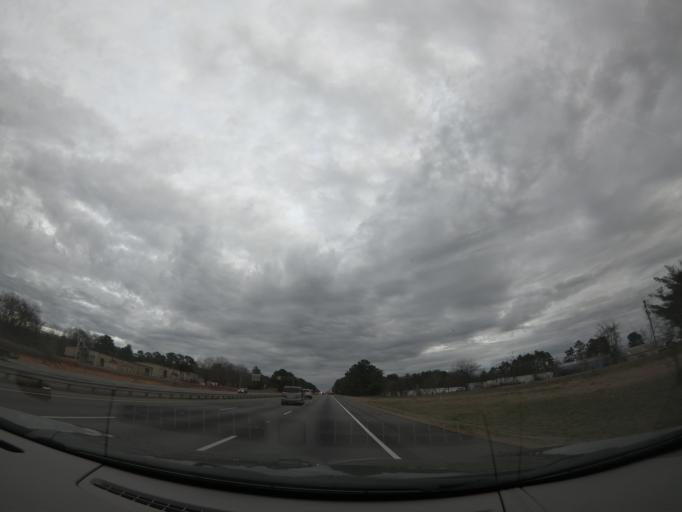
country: US
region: Georgia
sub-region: Catoosa County
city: Ringgold
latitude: 34.8912
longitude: -85.0723
